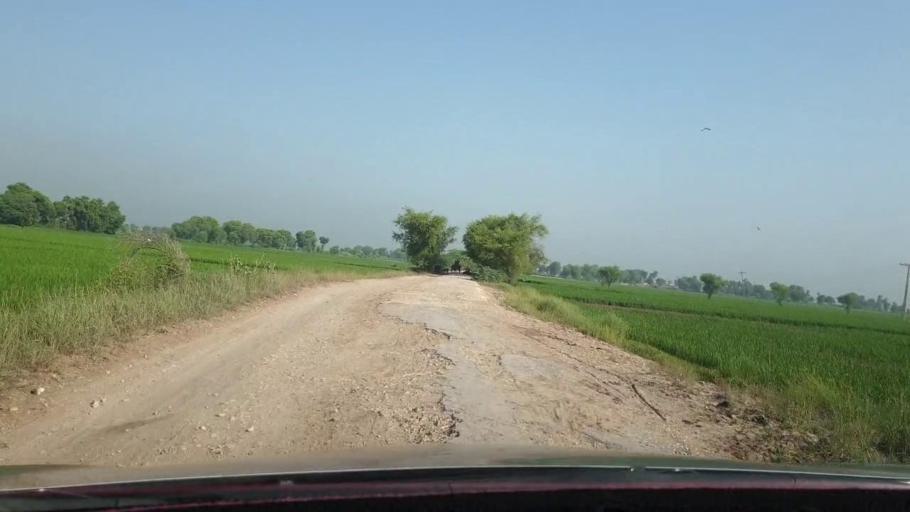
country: PK
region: Sindh
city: Nasirabad
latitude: 27.4437
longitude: 67.9198
